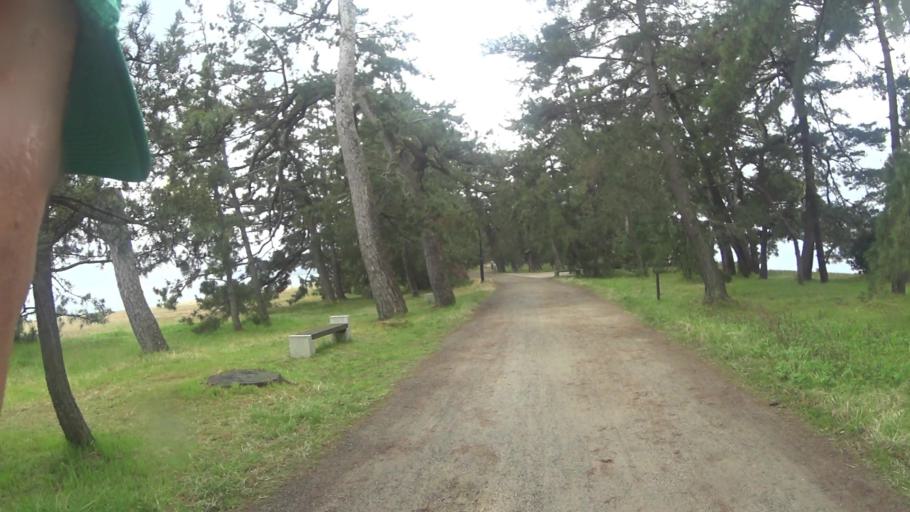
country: JP
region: Kyoto
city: Miyazu
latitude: 35.5761
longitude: 135.1986
